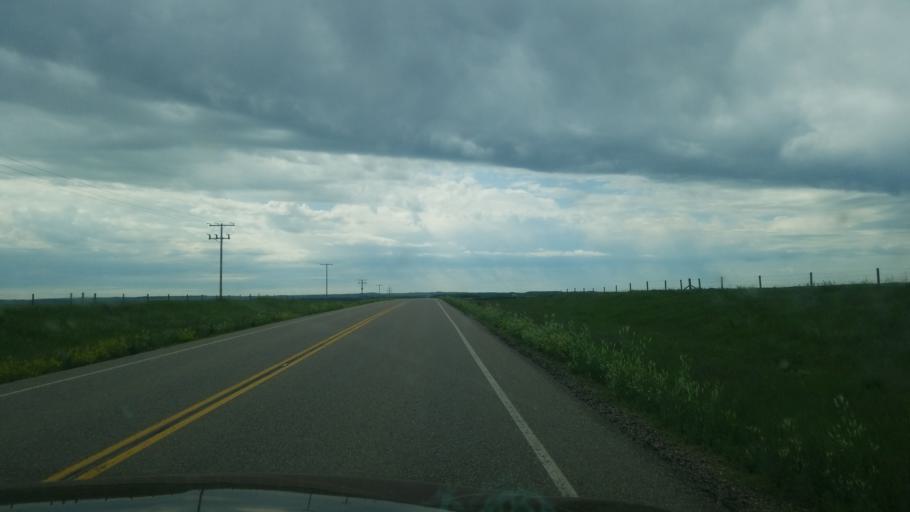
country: CA
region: Saskatchewan
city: Unity
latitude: 52.9698
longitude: -109.3426
